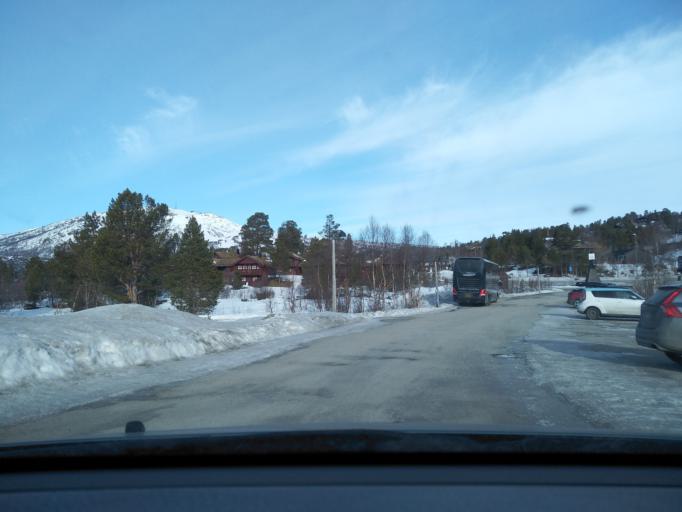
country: NO
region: Aust-Agder
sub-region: Bykle
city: Hovden
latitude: 59.5556
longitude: 7.3597
